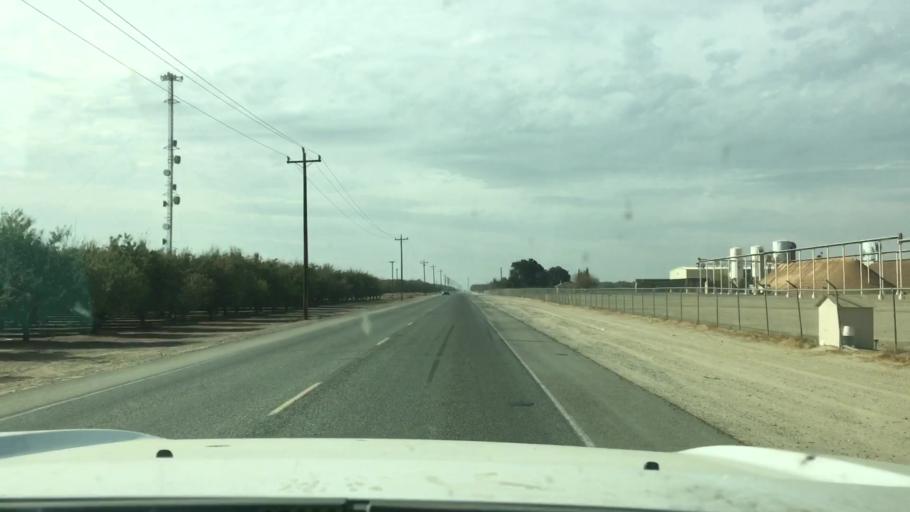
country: US
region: California
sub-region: Kern County
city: Buttonwillow
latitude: 35.5006
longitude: -119.5020
